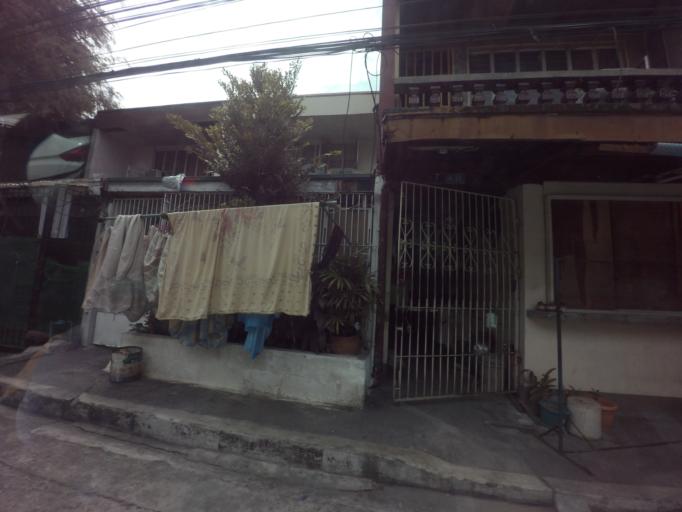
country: PH
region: Calabarzon
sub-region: Province of Rizal
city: Pateros
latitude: 14.5630
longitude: 121.0713
